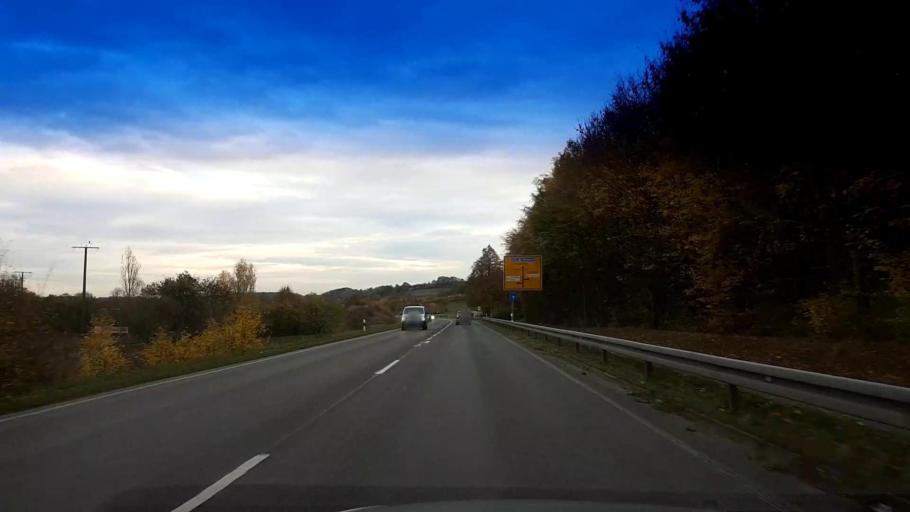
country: DE
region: Bavaria
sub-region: Regierungsbezirk Unterfranken
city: Stettfeld
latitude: 49.9388
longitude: 10.7314
